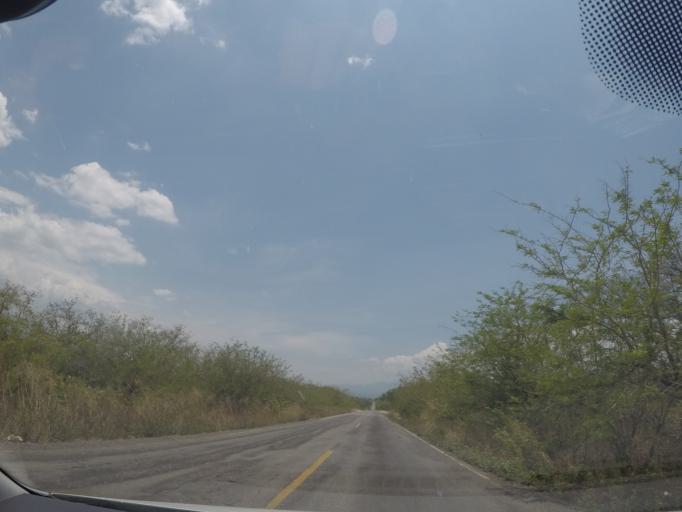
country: MX
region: Oaxaca
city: Santa Maria Jalapa del Marques
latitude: 16.4395
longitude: -95.4841
